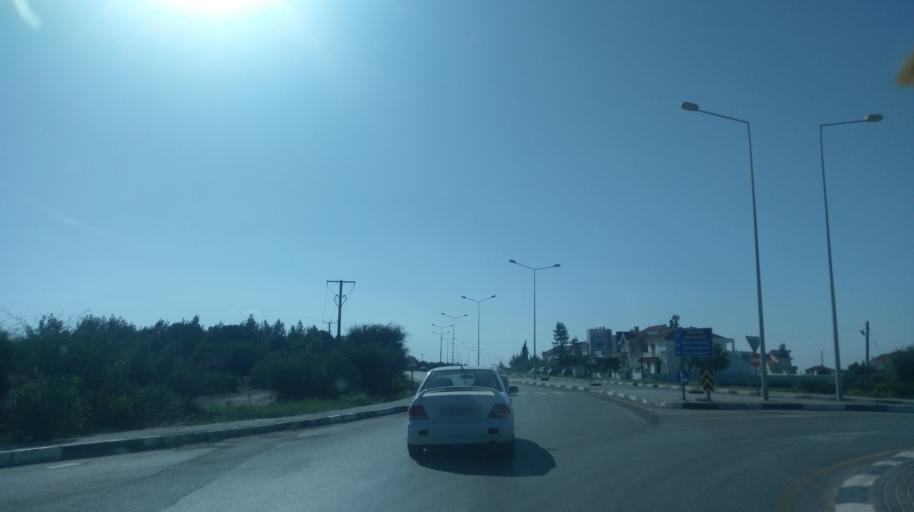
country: CY
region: Ammochostos
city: Trikomo
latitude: 35.2467
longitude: 33.9011
